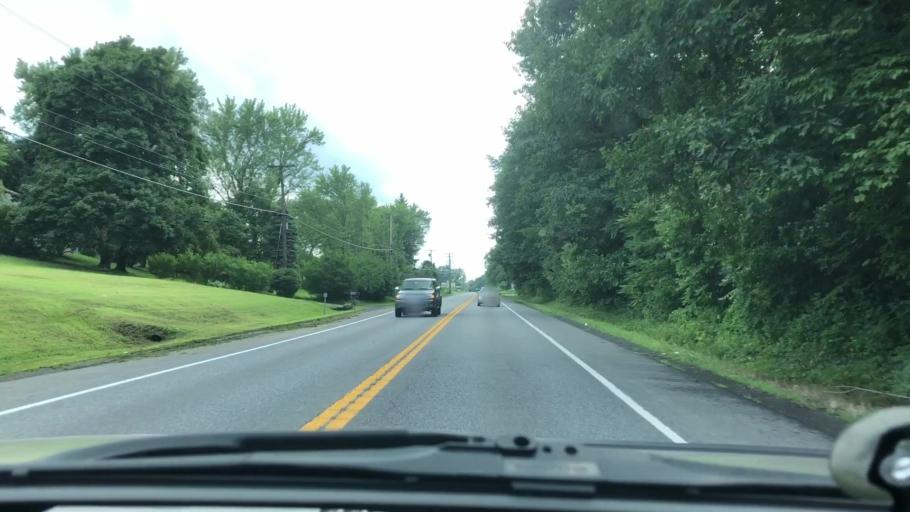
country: US
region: New York
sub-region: Ulster County
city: Saugerties
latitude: 42.1025
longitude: -73.9695
